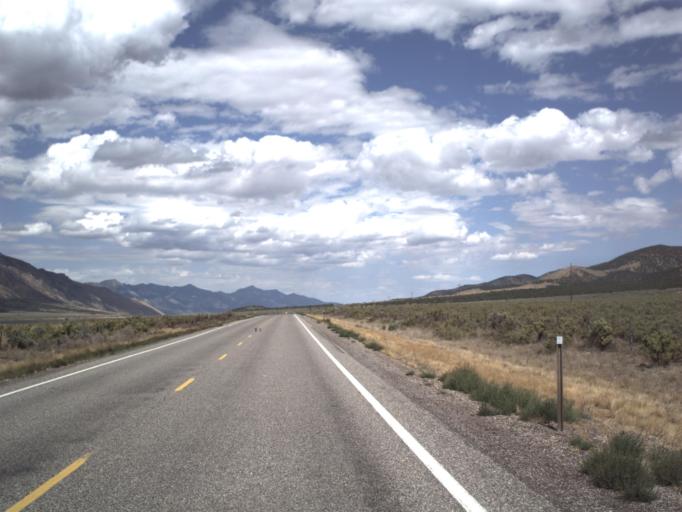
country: US
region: Utah
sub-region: Sevier County
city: Aurora
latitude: 39.1024
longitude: -112.0398
